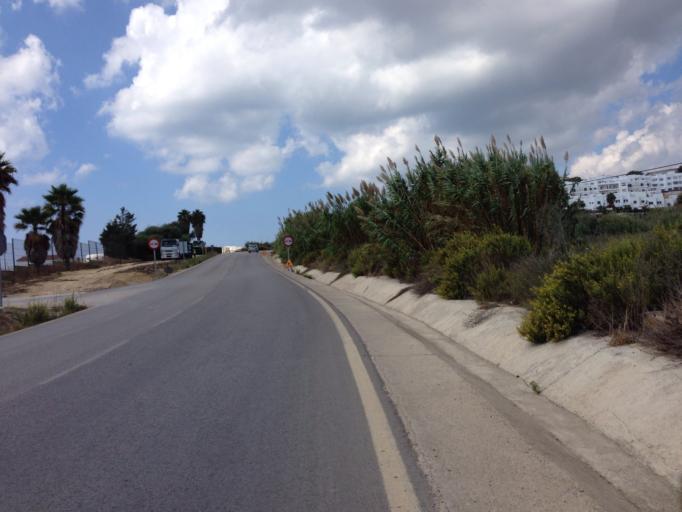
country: ES
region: Andalusia
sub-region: Provincia de Cadiz
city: Conil de la Frontera
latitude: 36.2762
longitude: -6.0765
